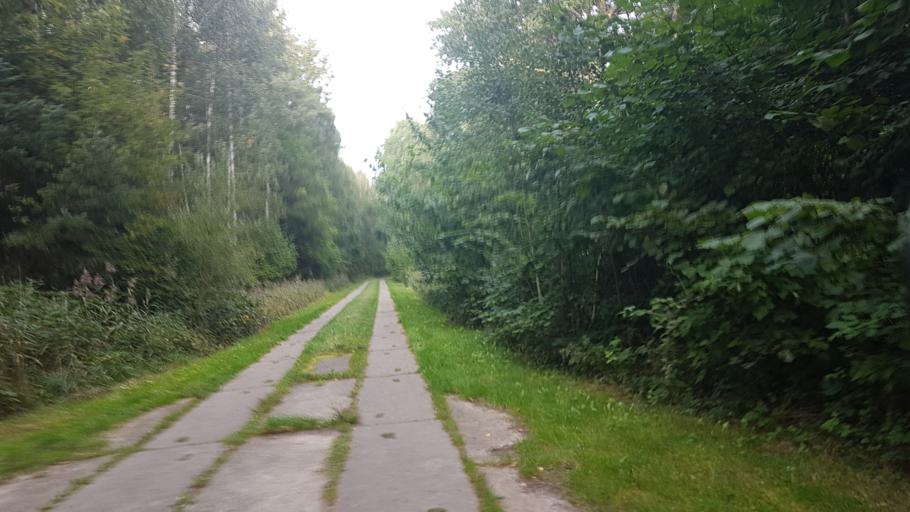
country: DE
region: Mecklenburg-Vorpommern
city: Gingst
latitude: 54.4805
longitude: 13.1806
